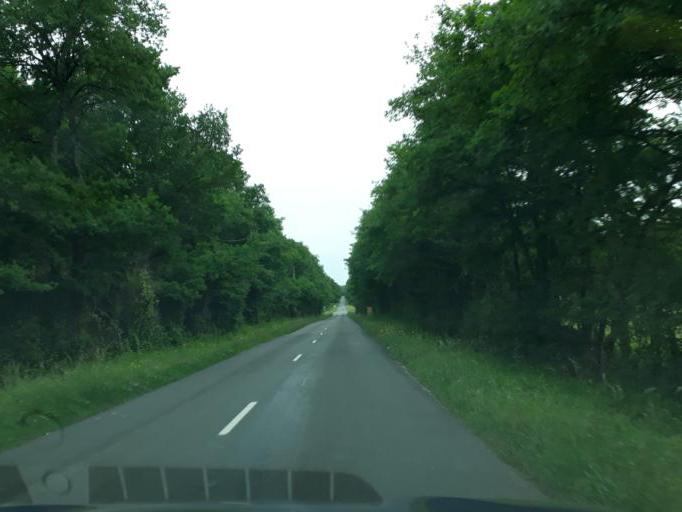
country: FR
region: Centre
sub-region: Departement du Loiret
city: Saint-Pere-sur-Loire
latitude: 47.7328
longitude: 2.3484
